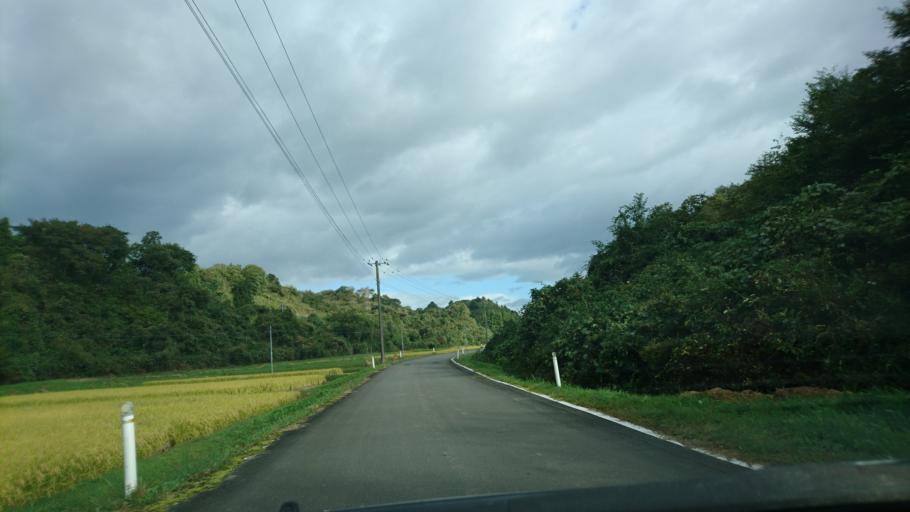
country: JP
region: Iwate
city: Ichinoseki
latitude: 38.8778
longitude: 141.0929
